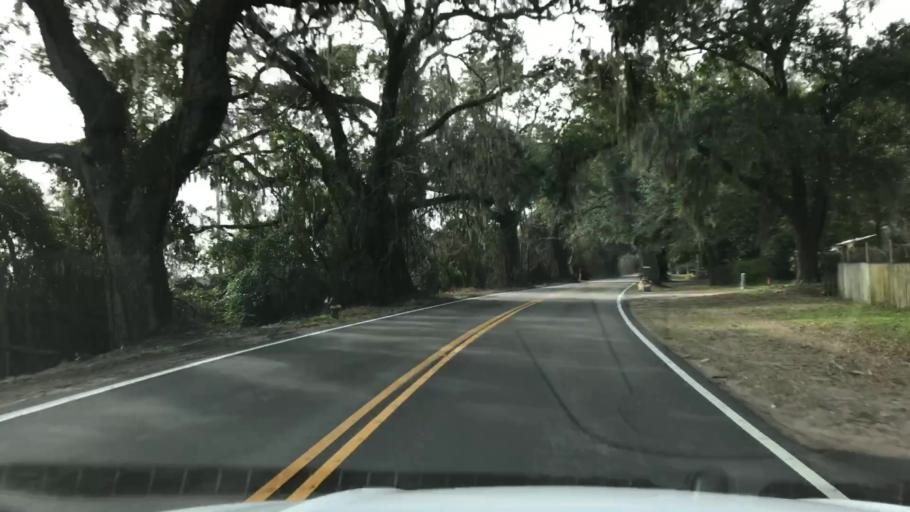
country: US
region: South Carolina
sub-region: Charleston County
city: Folly Beach
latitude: 32.6909
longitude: -80.0168
